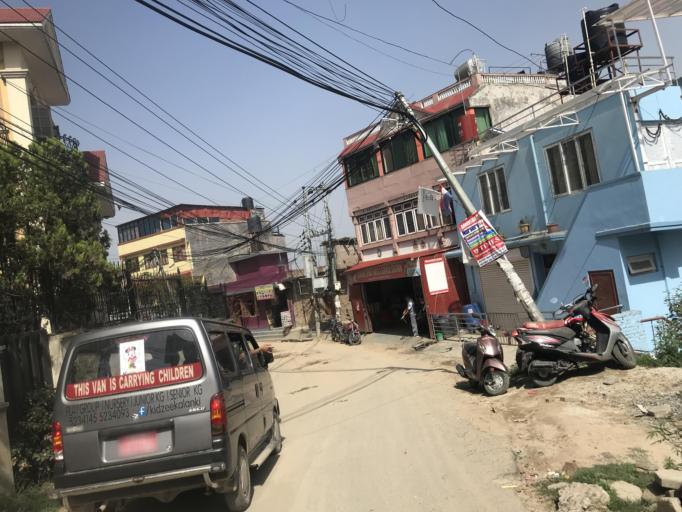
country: NP
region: Central Region
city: Kirtipur
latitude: 27.6865
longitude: 85.2831
